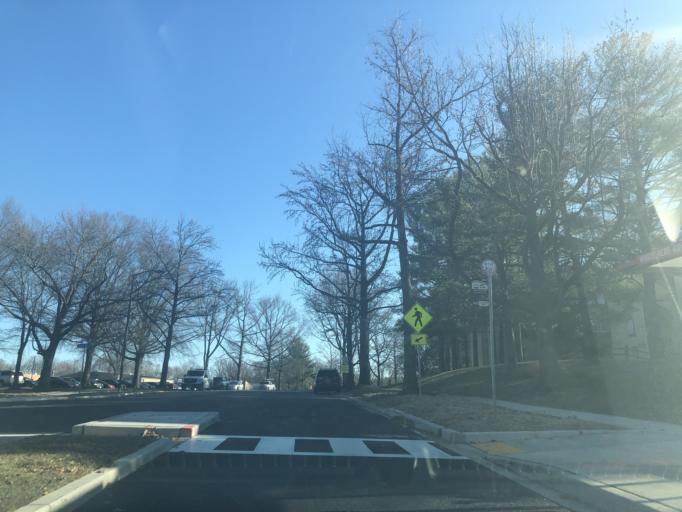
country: US
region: Maryland
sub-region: Howard County
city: Columbia
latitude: 39.2121
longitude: -76.8458
